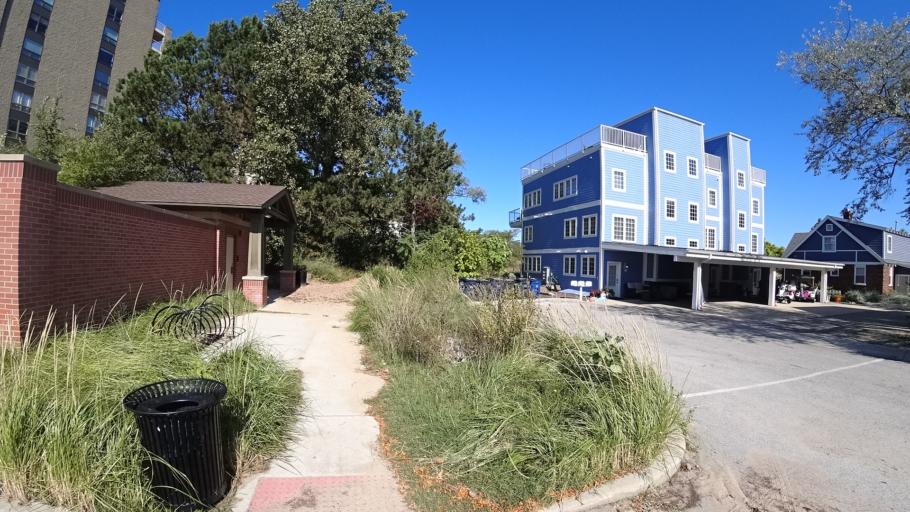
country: US
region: Indiana
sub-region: LaPorte County
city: Michigan City
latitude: 41.7300
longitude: -86.8934
